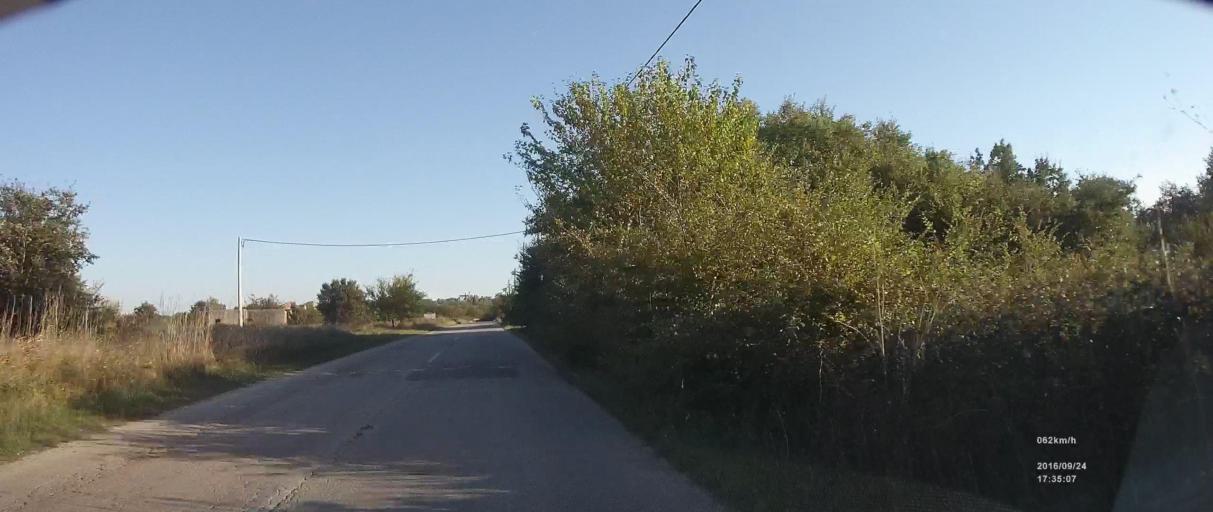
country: HR
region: Zadarska
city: Posedarje
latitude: 44.1629
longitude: 15.4651
